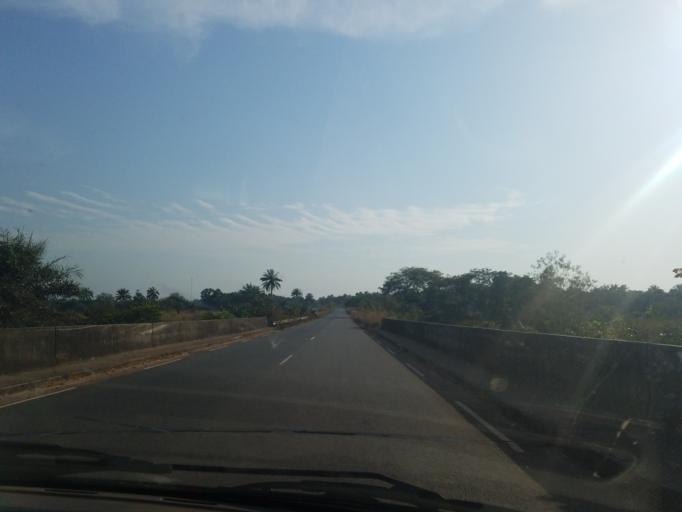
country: GN
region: Boke
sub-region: Boke Prefecture
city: Sangueya
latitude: 10.4983
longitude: -14.4054
